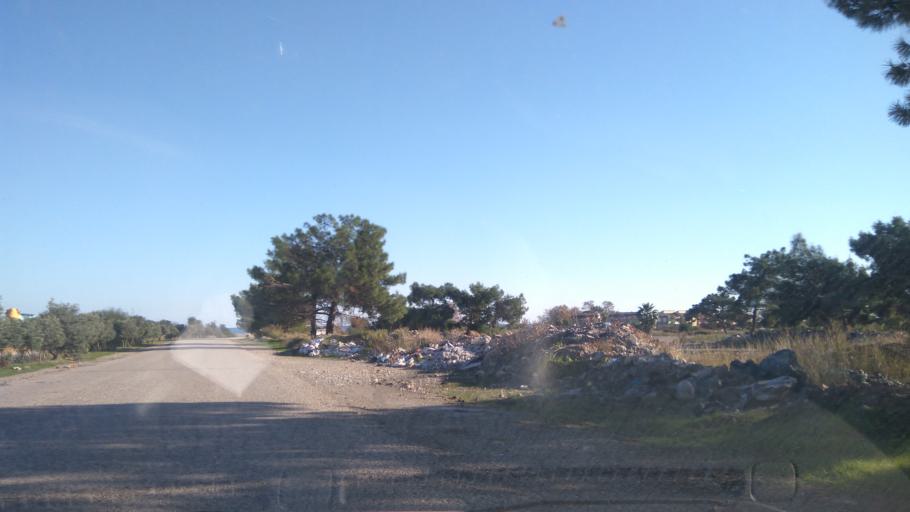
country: TR
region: Antalya
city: Kemer
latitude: 36.5659
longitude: 30.5688
